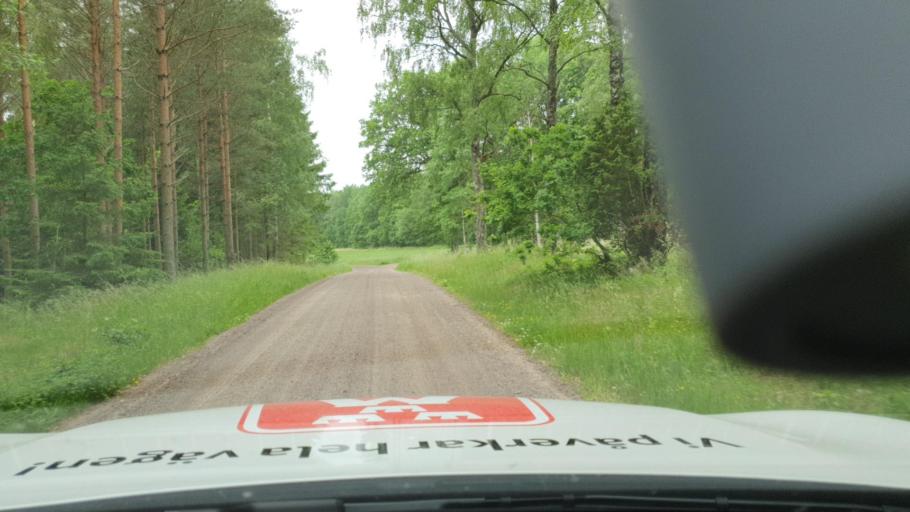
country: SE
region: Vaestra Goetaland
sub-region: Hjo Kommun
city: Hjo
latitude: 58.3641
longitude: 14.3466
